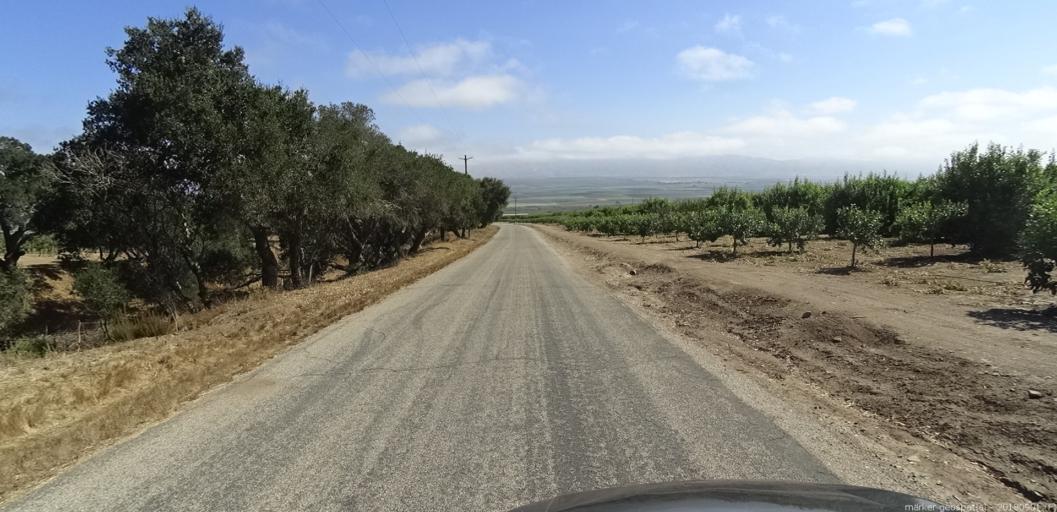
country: US
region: California
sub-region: Monterey County
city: Gonzales
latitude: 36.4432
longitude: -121.4557
